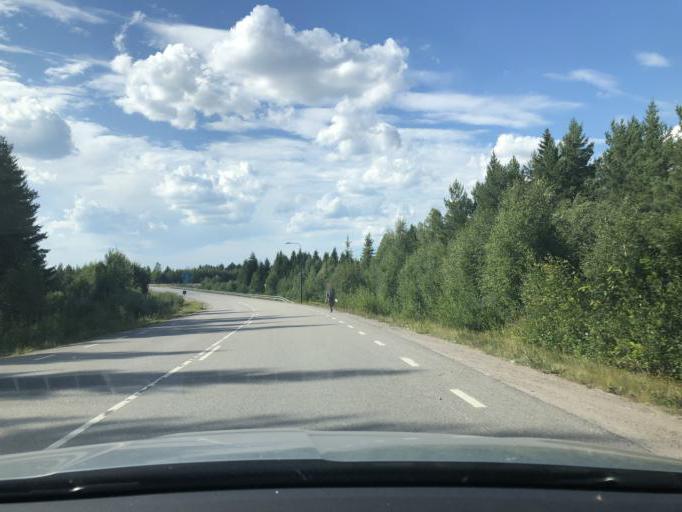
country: SE
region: Uppsala
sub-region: Tierps Kommun
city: Tierp
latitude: 60.2144
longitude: 17.5018
